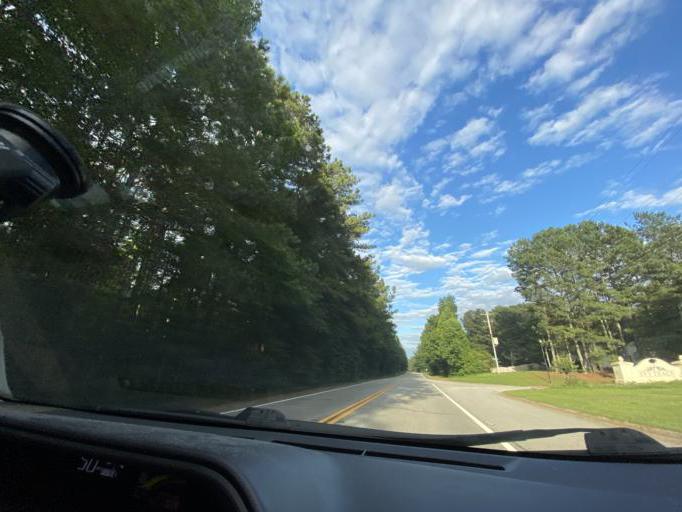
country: US
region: Georgia
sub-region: Fulton County
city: Palmetto
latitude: 33.4461
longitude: -84.6804
